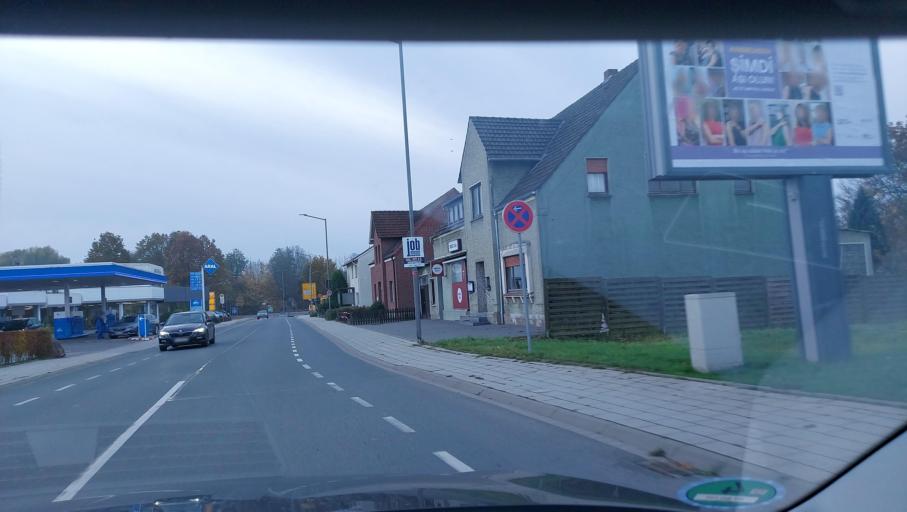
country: DE
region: North Rhine-Westphalia
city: Spenge
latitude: 52.1487
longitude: 8.4849
